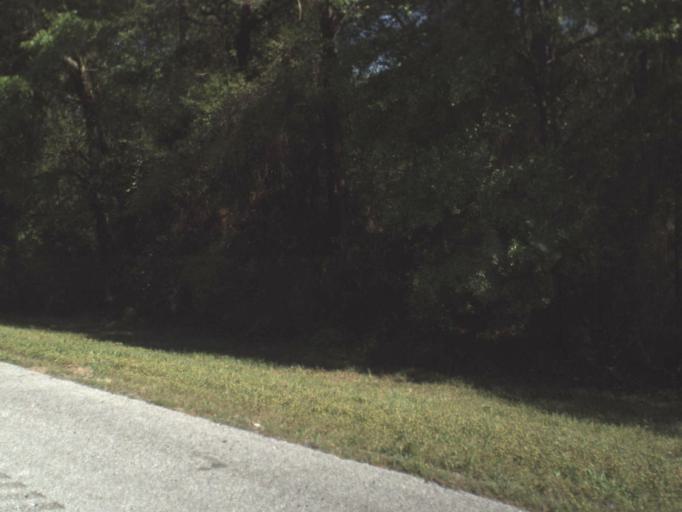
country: US
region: Florida
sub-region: Okaloosa County
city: Crestview
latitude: 30.7080
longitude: -86.7205
